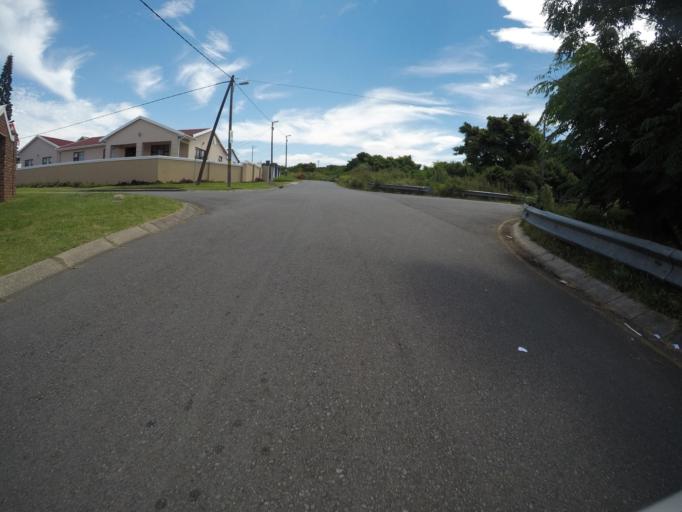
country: ZA
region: Eastern Cape
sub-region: Buffalo City Metropolitan Municipality
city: East London
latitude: -33.0411
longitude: 27.8667
